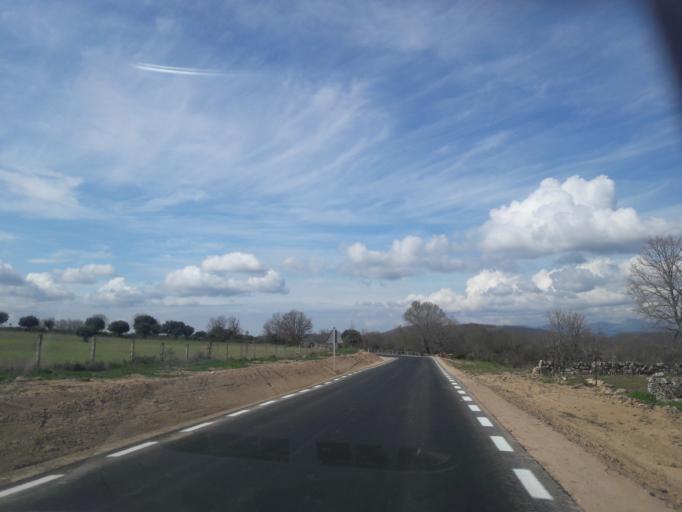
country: ES
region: Castille and Leon
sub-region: Provincia de Salamanca
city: Monleon
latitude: 40.5256
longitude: -5.8387
